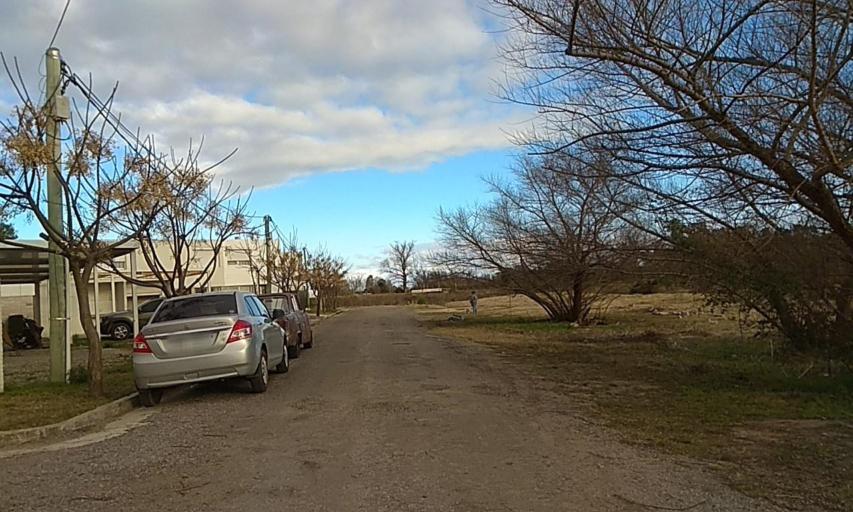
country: UY
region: Florida
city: Florida
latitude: -34.1012
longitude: -56.2231
